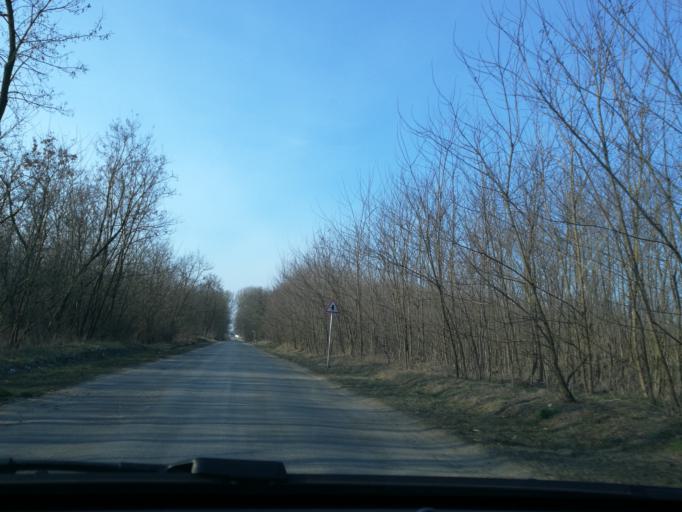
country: HU
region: Szabolcs-Szatmar-Bereg
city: Levelek
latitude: 48.0299
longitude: 21.9688
